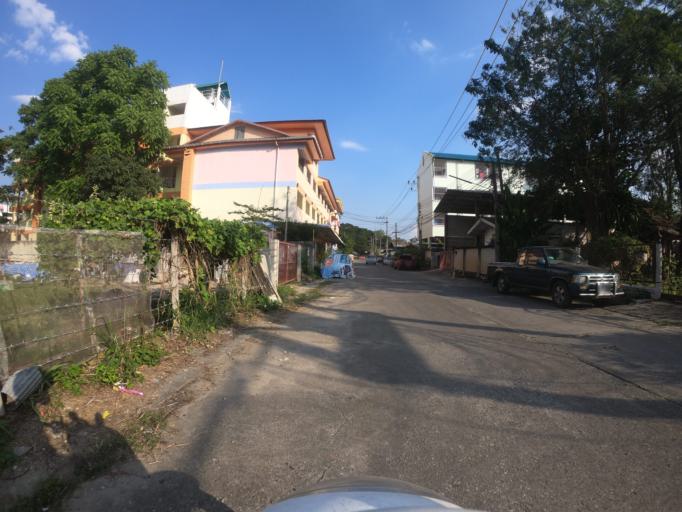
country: TH
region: Chiang Mai
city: Chiang Mai
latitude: 18.8173
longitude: 98.9722
